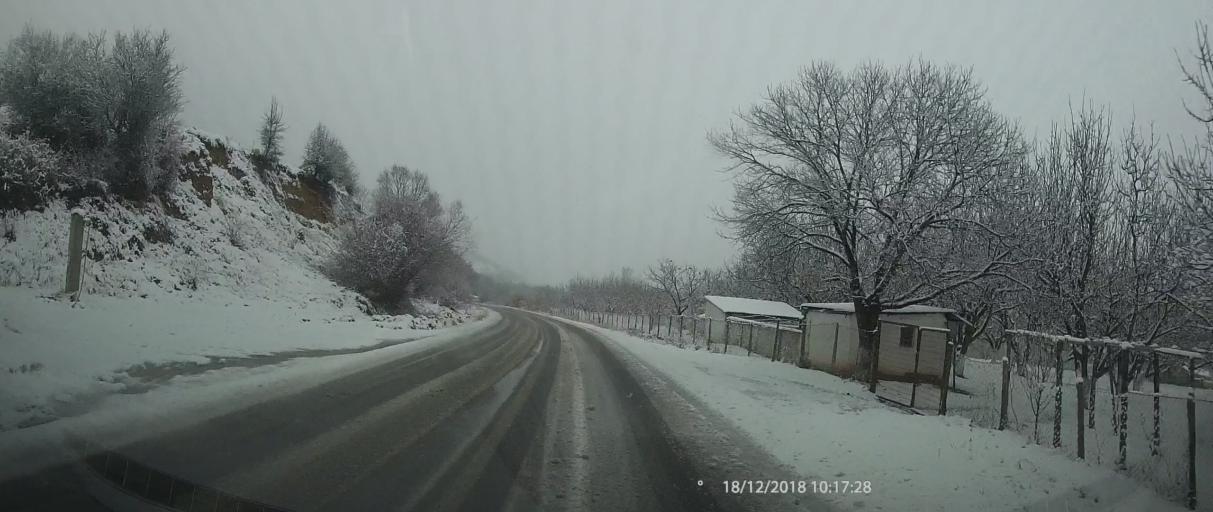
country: GR
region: Thessaly
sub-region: Nomos Larisis
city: Livadi
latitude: 40.1241
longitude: 22.2133
